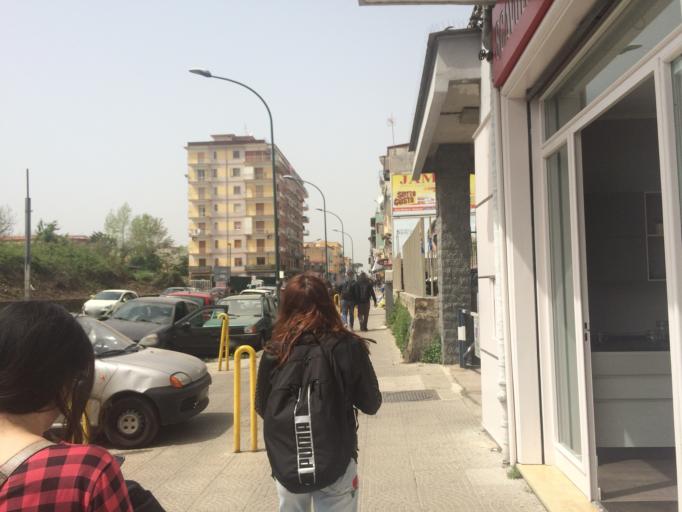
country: IT
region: Campania
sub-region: Provincia di Napoli
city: Mugnano di Napoli
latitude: 40.8913
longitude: 14.2219
